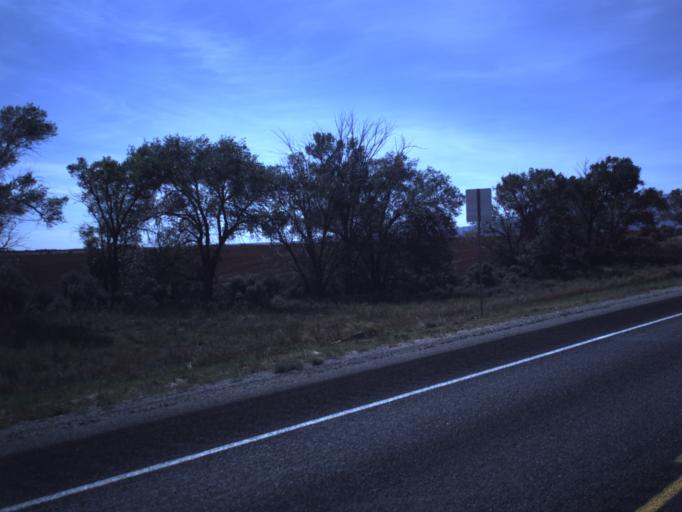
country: US
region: Utah
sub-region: San Juan County
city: Monticello
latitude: 37.8463
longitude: -109.1481
